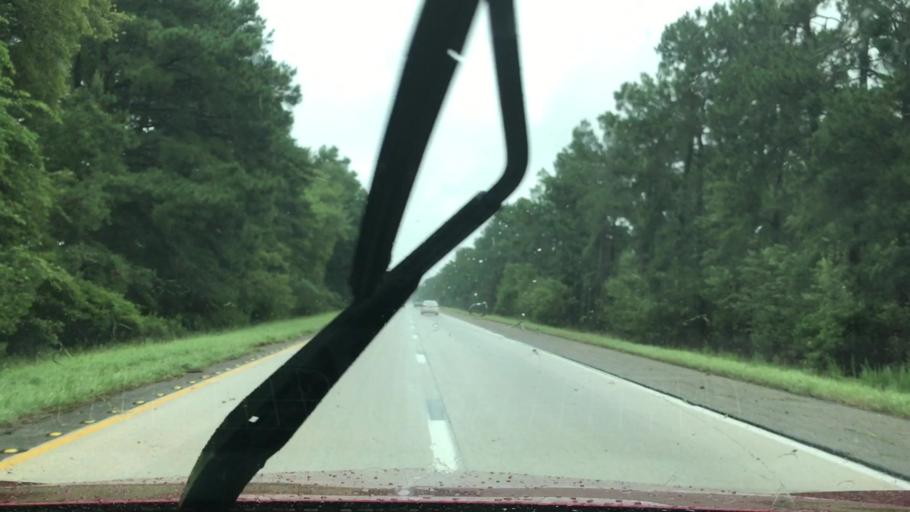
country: US
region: South Carolina
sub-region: Orangeburg County
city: Holly Hill
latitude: 33.2088
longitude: -80.4096
